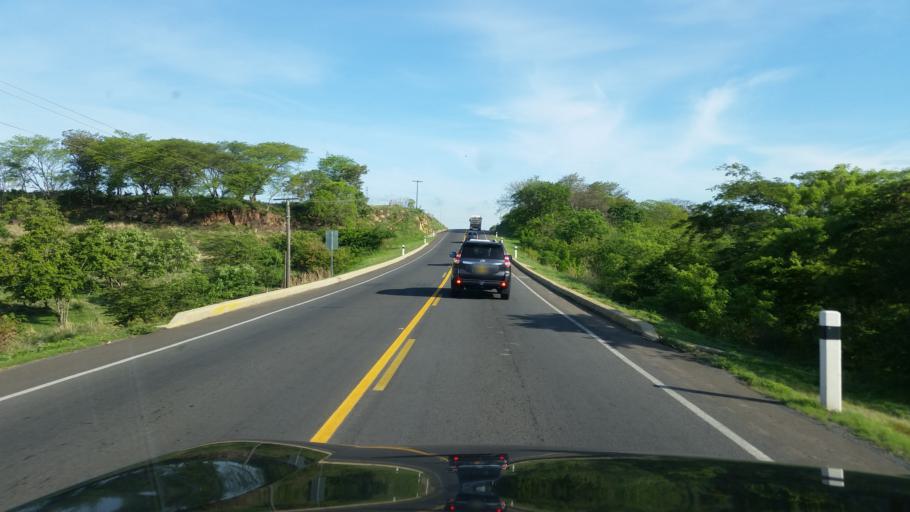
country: NI
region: Leon
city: La Paz Centro
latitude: 12.2312
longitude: -86.7037
